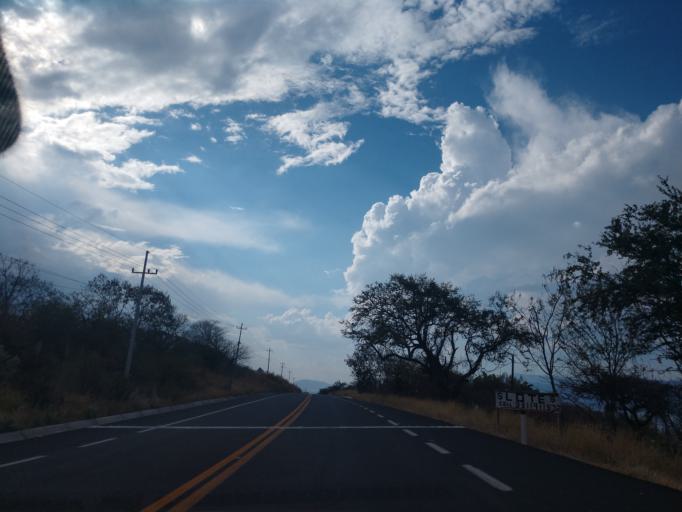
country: MX
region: Jalisco
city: Ajijic
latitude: 20.1897
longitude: -103.2561
